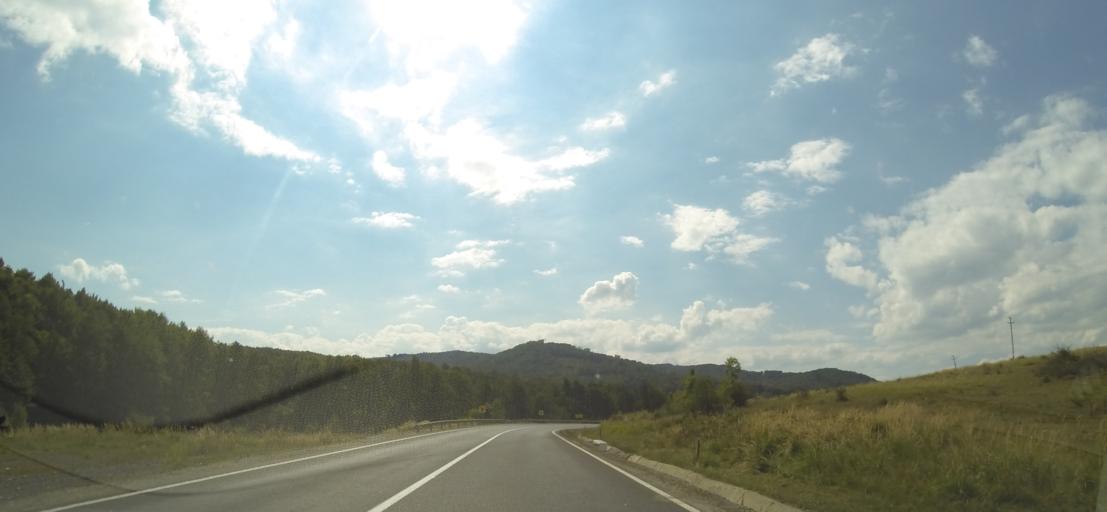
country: RO
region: Brasov
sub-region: Comuna Sinca Noua
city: Sinca Noua
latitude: 45.7520
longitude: 25.2687
